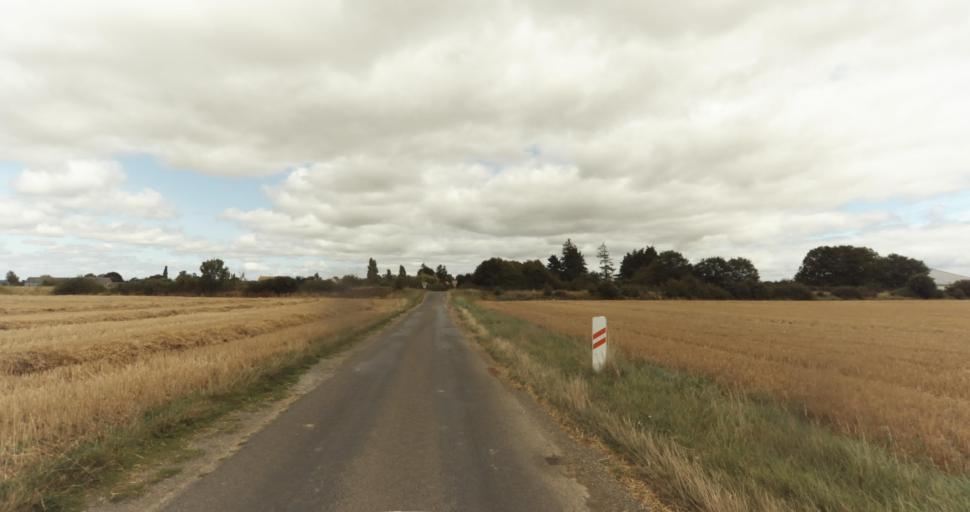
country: FR
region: Haute-Normandie
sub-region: Departement de l'Eure
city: Marcilly-sur-Eure
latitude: 48.9182
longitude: 1.2474
